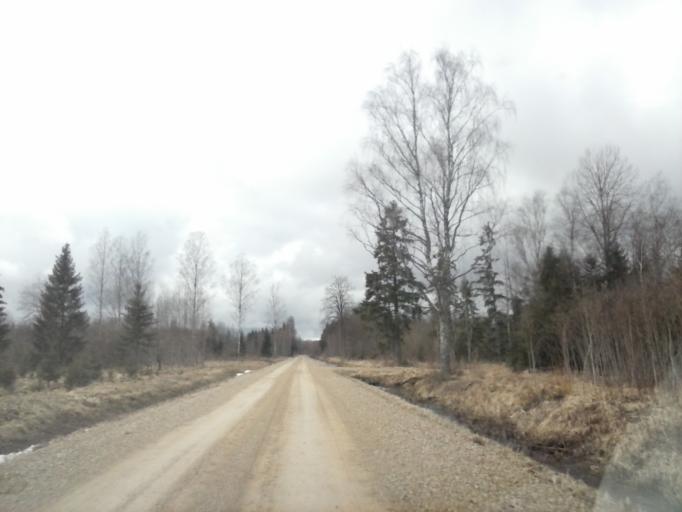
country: EE
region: Jogevamaa
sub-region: Mustvee linn
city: Mustvee
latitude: 59.0950
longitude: 26.8307
